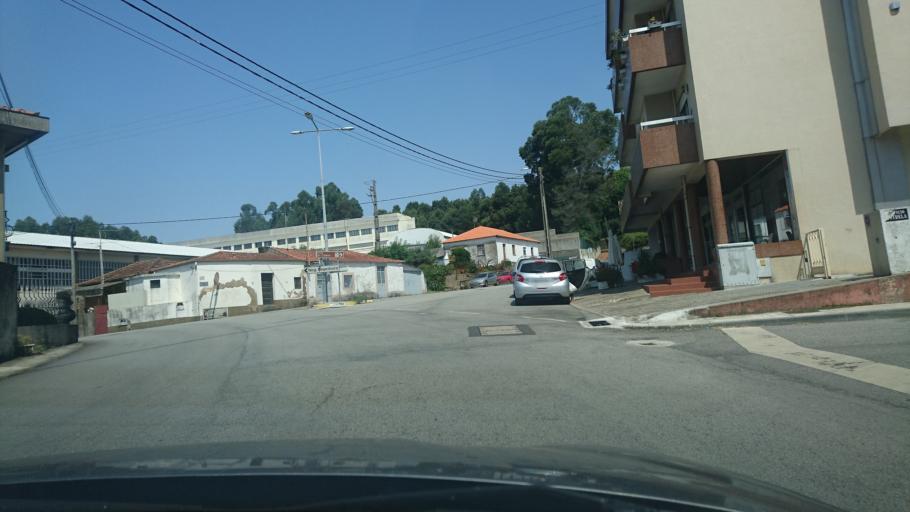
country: PT
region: Aveiro
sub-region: Santa Maria da Feira
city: Lamas
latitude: 40.9948
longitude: -8.5728
